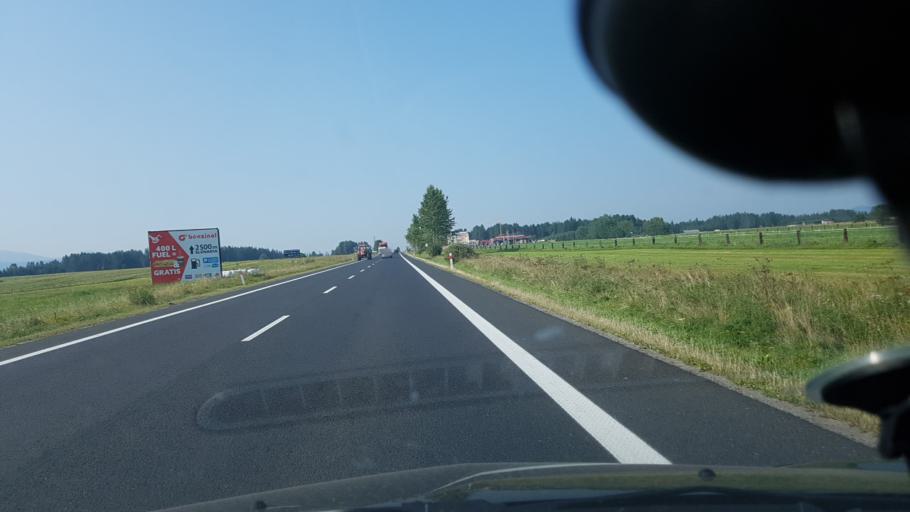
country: PL
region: Lesser Poland Voivodeship
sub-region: Powiat nowotarski
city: Chyzne
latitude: 49.4212
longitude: 19.6699
